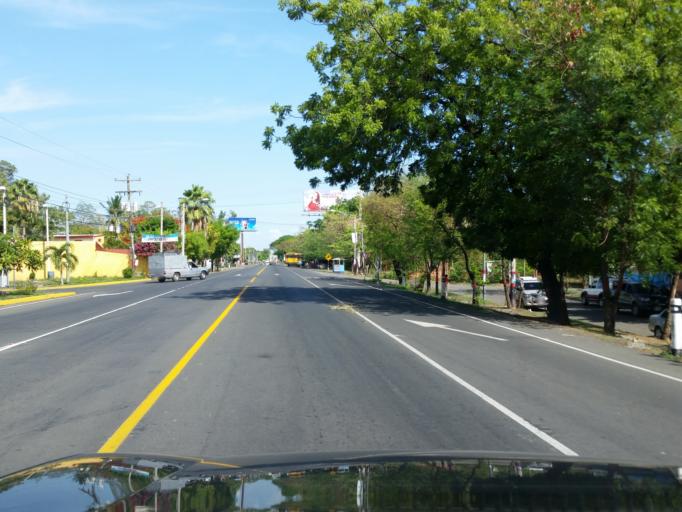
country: NI
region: Leon
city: Leon
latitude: 12.4204
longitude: -86.8714
